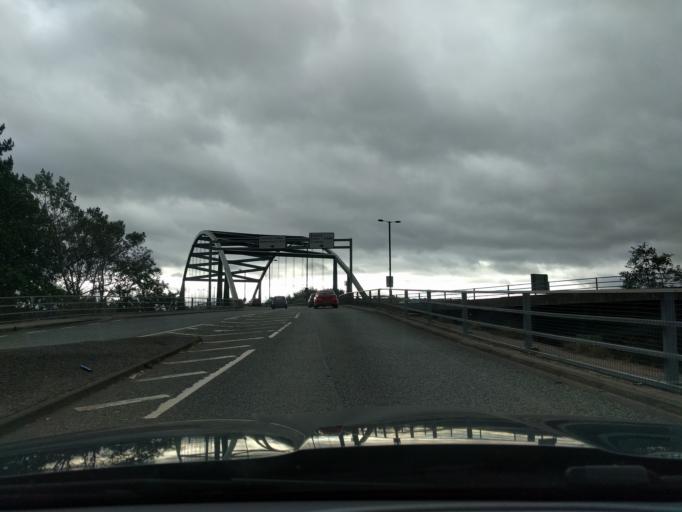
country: GB
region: England
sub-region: Newcastle upon Tyne
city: Benwell
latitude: 54.9679
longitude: -1.6887
